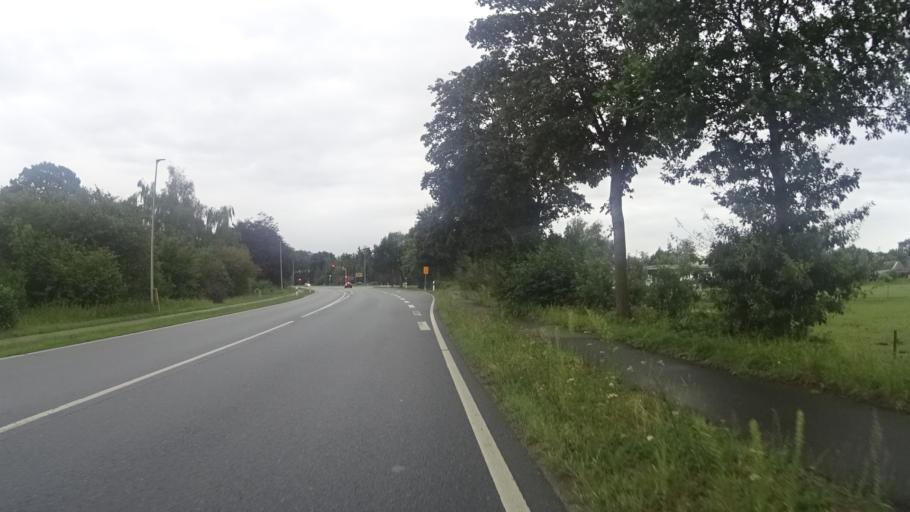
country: DE
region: Schleswig-Holstein
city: Kiebitzreihe
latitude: 53.7831
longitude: 9.6381
